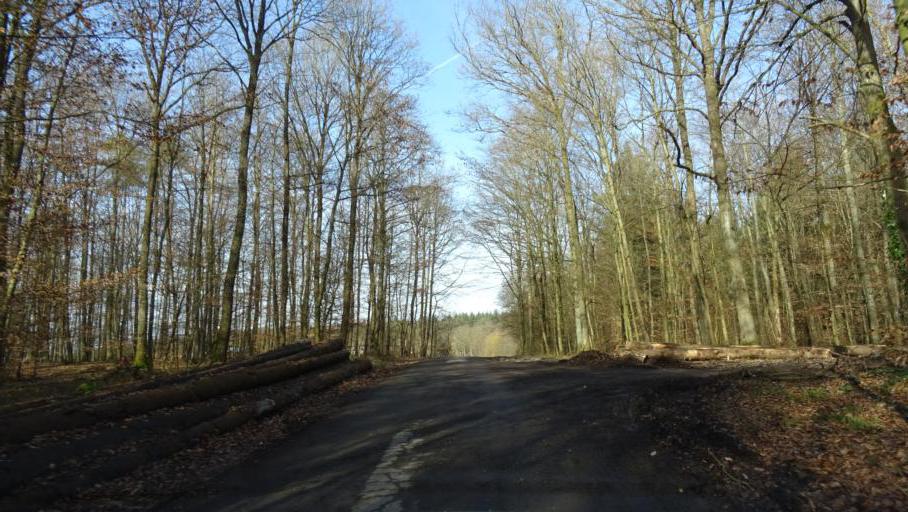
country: DE
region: Baden-Wuerttemberg
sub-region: Karlsruhe Region
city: Billigheim
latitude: 49.3685
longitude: 9.2434
